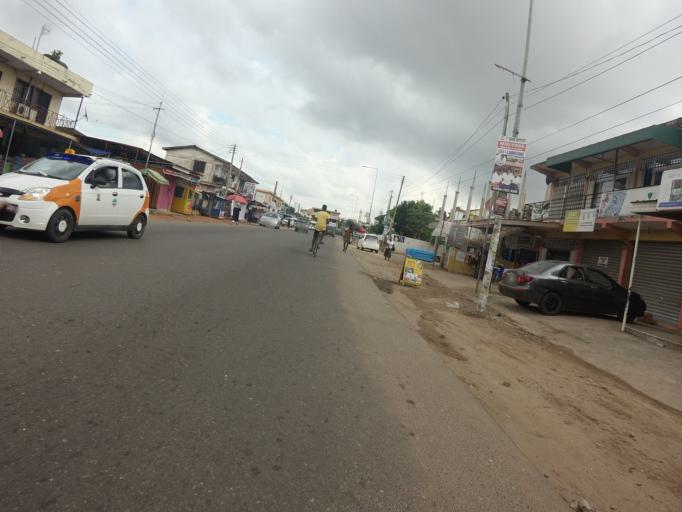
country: GH
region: Greater Accra
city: Accra
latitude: 5.5913
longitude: -0.2061
